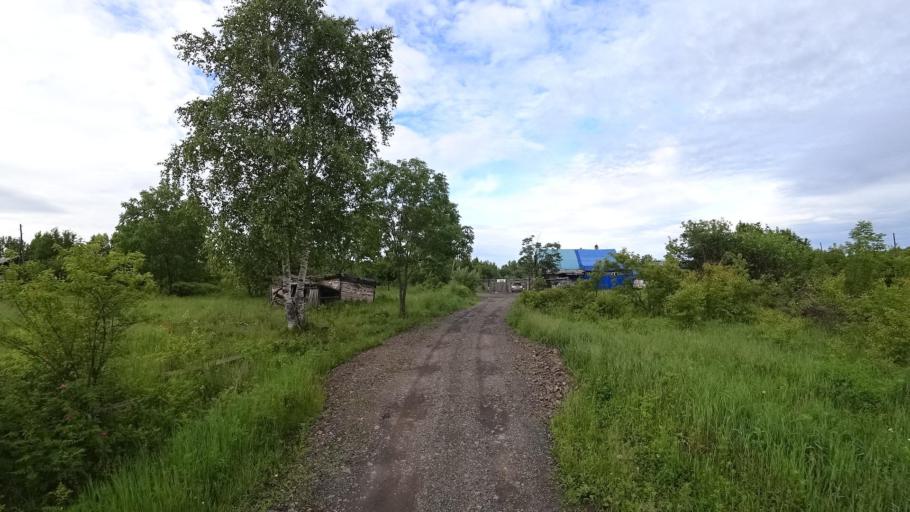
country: RU
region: Khabarovsk Krai
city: Amursk
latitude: 49.8924
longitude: 136.1269
